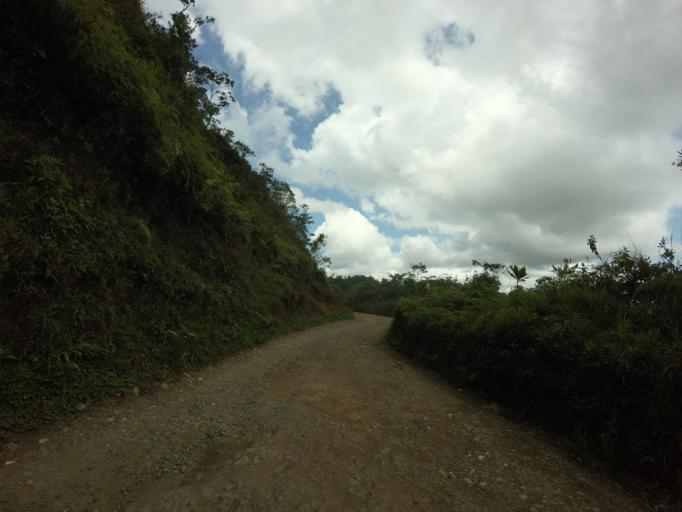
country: CO
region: Caldas
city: Victoria
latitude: 5.3079
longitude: -74.9691
